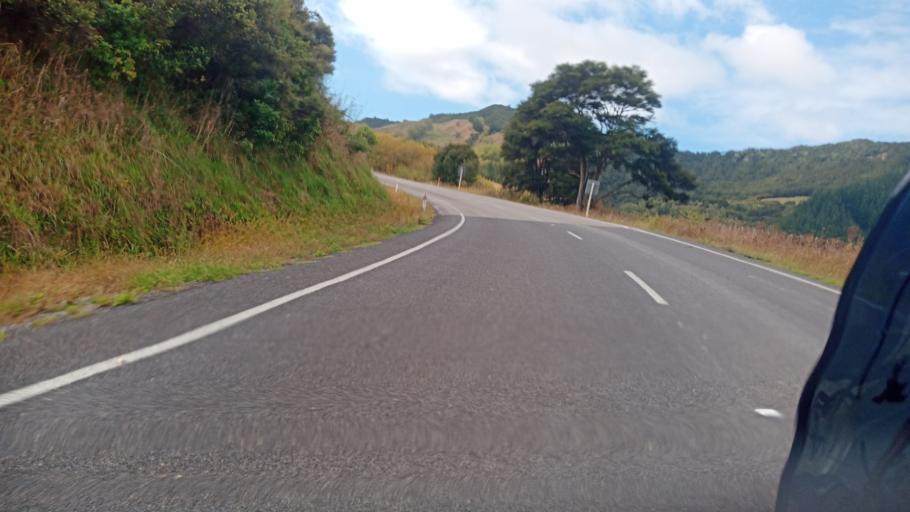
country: NZ
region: Gisborne
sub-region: Gisborne District
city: Gisborne
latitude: -38.1594
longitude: 178.2808
